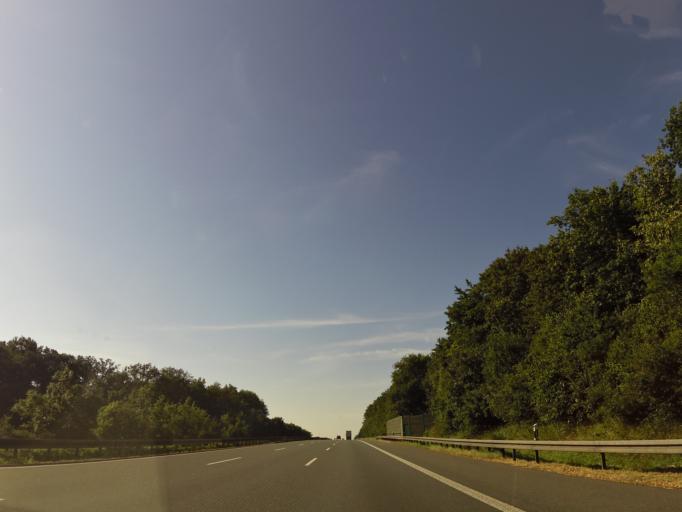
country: DE
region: Bavaria
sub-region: Regierungsbezirk Mittelfranken
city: Allersberg
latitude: 49.2284
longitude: 11.2226
